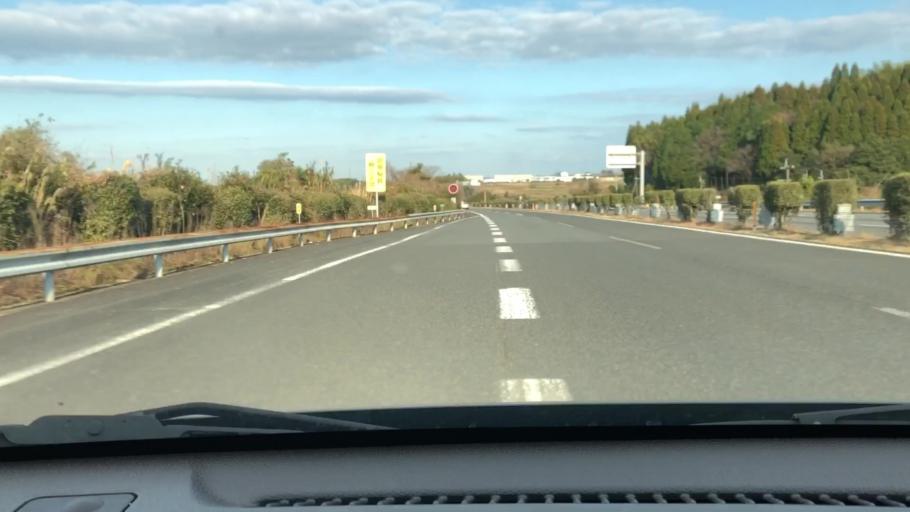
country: JP
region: Miyazaki
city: Miyazaki-shi
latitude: 31.8228
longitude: 131.3052
